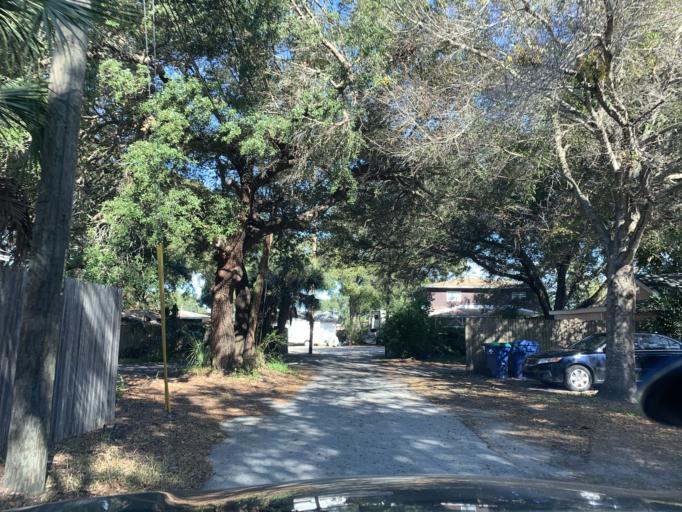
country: US
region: Florida
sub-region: Pinellas County
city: Kenneth City
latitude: 27.8149
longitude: -82.7469
